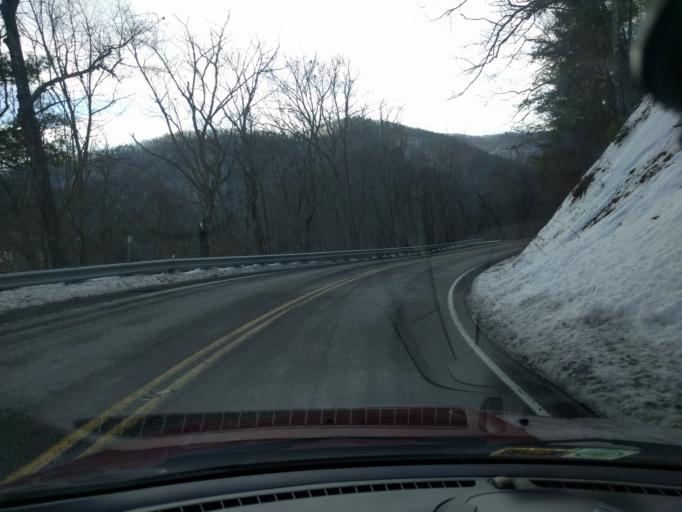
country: US
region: Virginia
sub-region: Bath County
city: Warm Springs
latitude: 38.1212
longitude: -79.9395
